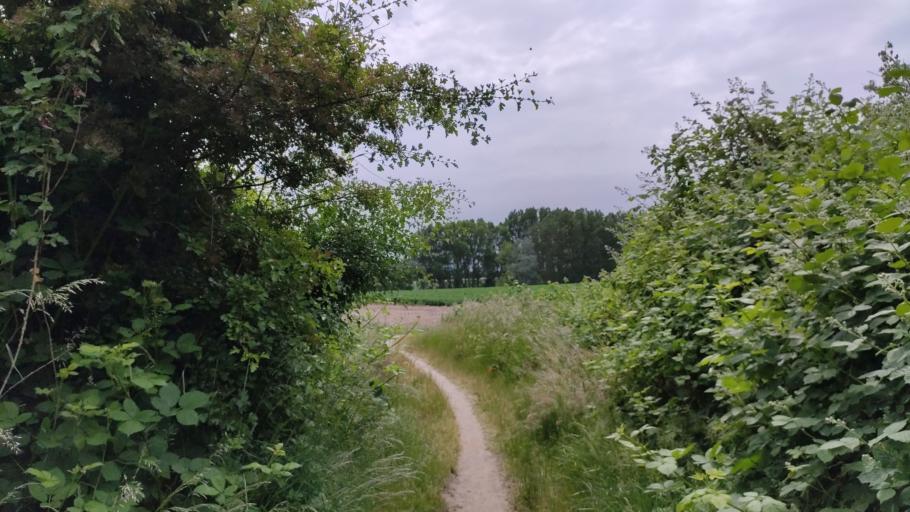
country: DE
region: Mecklenburg-Vorpommern
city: Bastorf
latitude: 54.1302
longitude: 11.6490
